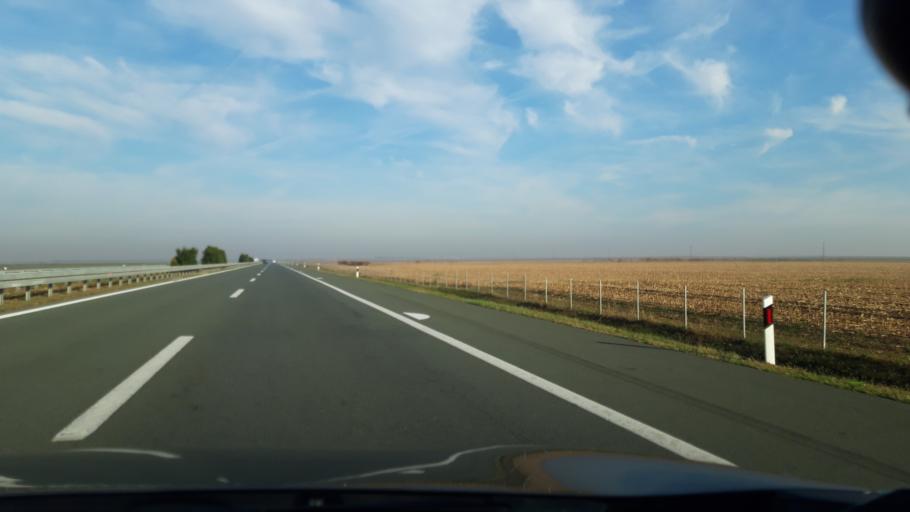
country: RS
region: Autonomna Pokrajina Vojvodina
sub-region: Juznobacki Okrug
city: Vrbas
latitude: 45.5913
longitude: 19.7150
